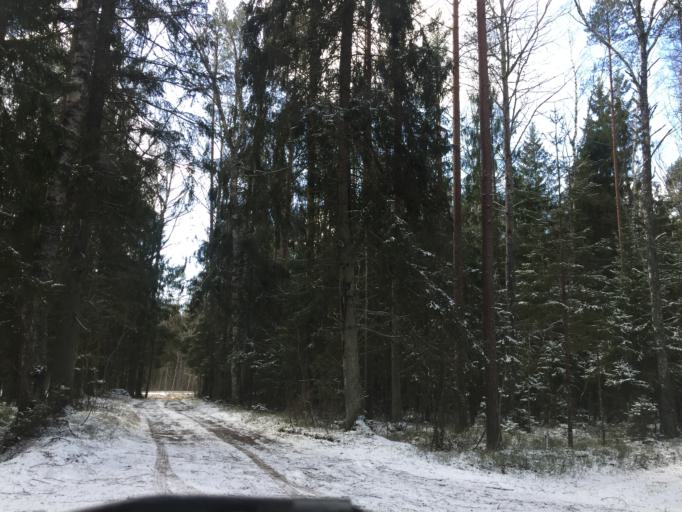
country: LV
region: Engure
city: Smarde
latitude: 56.9242
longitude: 23.4153
